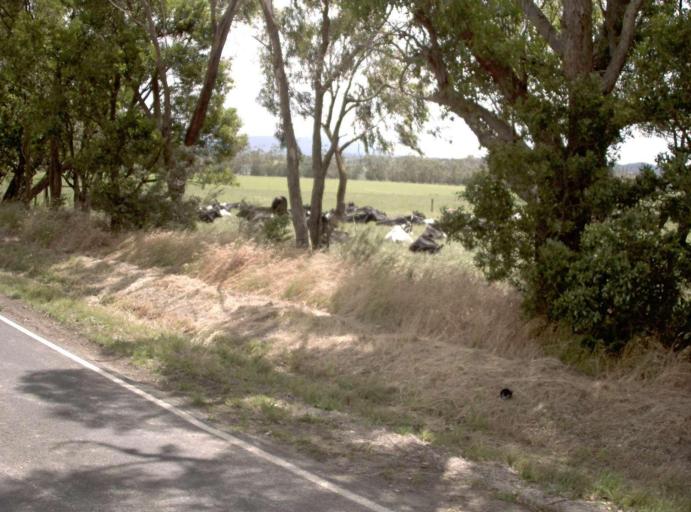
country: AU
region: Victoria
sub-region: Latrobe
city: Moe
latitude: -38.1008
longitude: 146.1576
